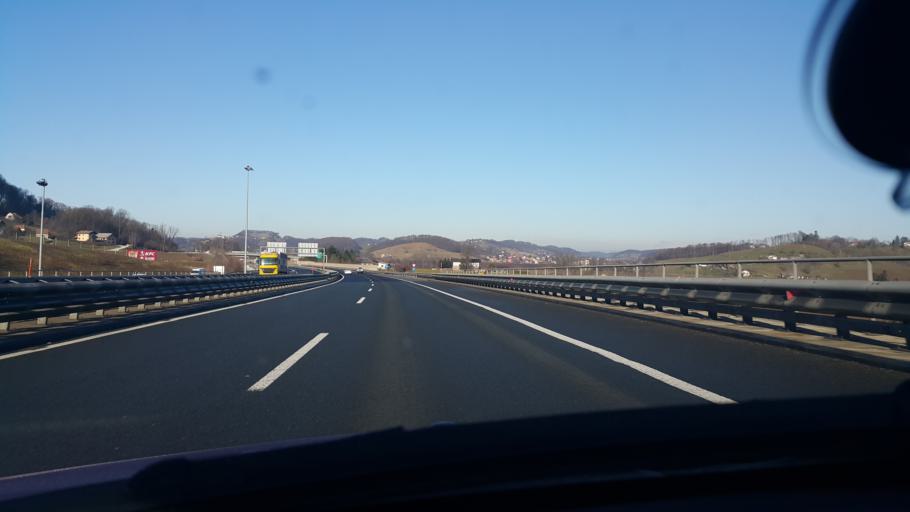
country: SI
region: Pesnica
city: Pesnica pri Mariboru
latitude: 46.5876
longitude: 15.6867
